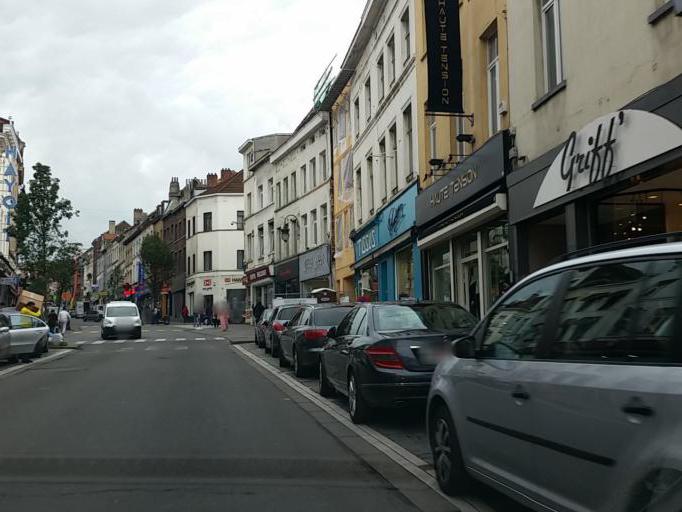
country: BE
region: Brussels Capital
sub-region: Bruxelles-Capitale
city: Brussels
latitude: 50.8293
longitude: 4.3444
